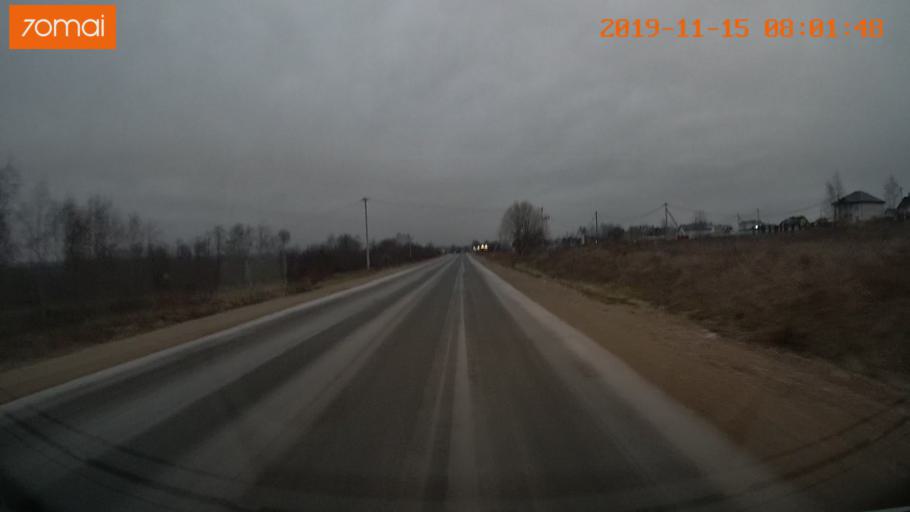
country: RU
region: Vologda
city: Cherepovets
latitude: 58.9793
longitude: 38.1079
